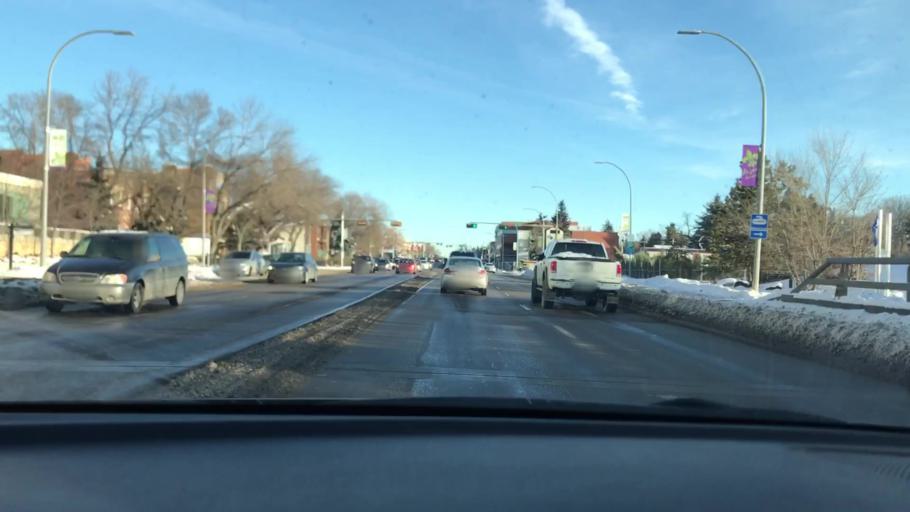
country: CA
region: Alberta
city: Edmonton
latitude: 53.5180
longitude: -113.4719
